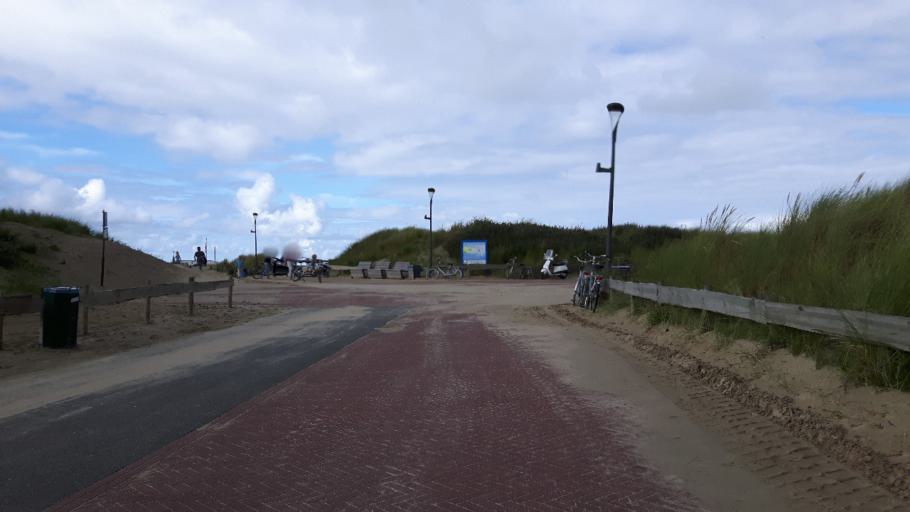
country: NL
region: Friesland
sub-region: Gemeente Ameland
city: Hollum
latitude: 53.4497
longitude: 5.6166
